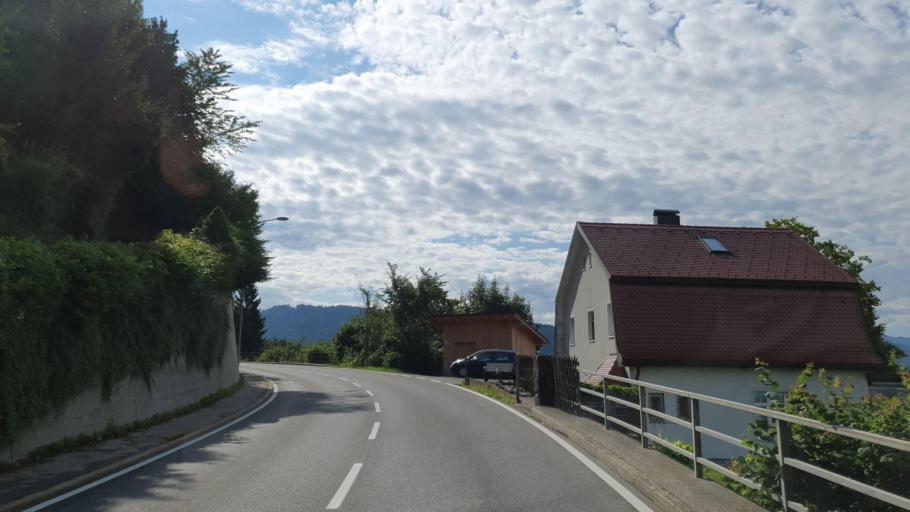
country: AT
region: Vorarlberg
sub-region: Politischer Bezirk Bregenz
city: Bregenz
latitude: 47.4870
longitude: 9.7495
